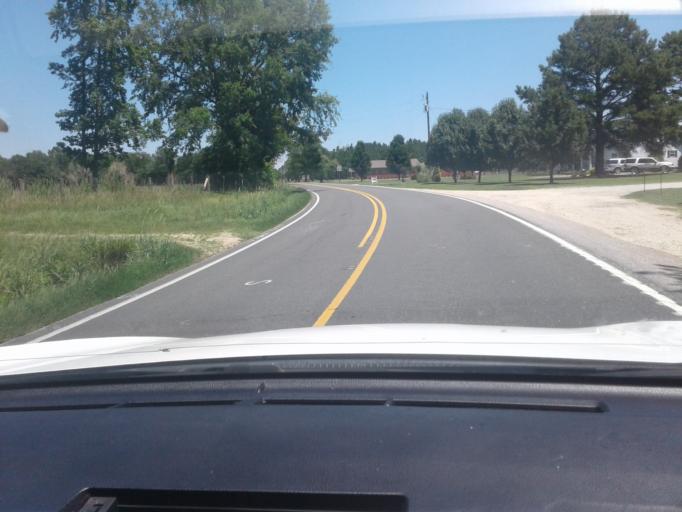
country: US
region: North Carolina
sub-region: Harnett County
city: Lillington
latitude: 35.3894
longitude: -78.7943
